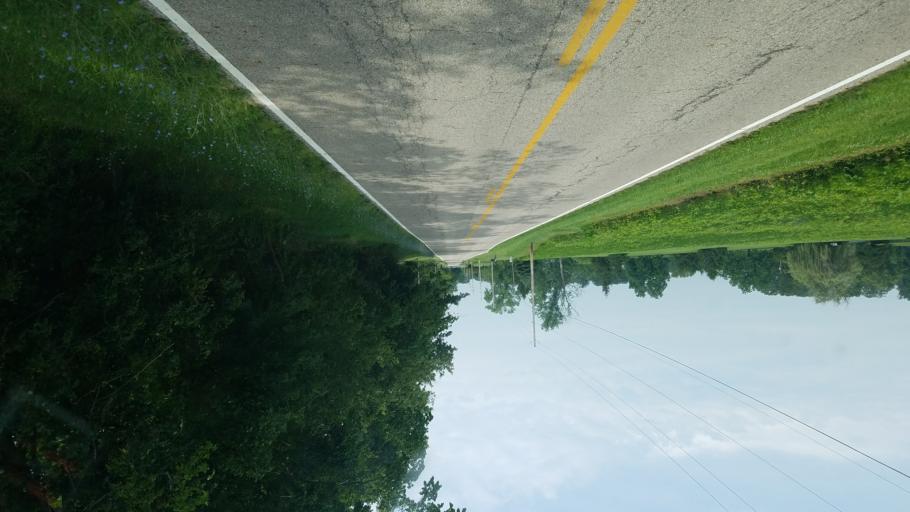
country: US
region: Ohio
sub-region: Madison County
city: West Jefferson
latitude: 39.9040
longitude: -83.2594
